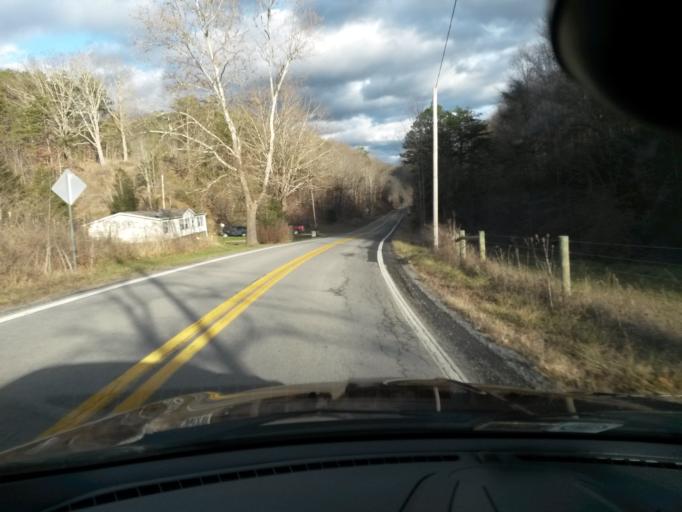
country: US
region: West Virginia
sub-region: Monroe County
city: Union
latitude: 37.4795
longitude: -80.6276
